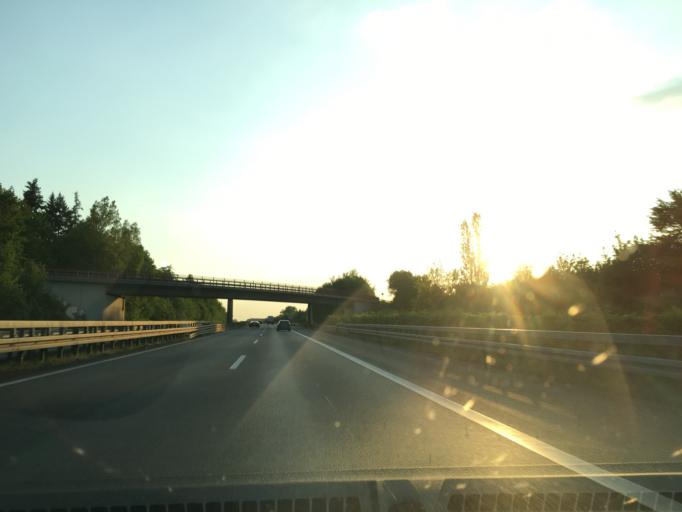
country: DE
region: North Rhine-Westphalia
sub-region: Regierungsbezirk Detmold
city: Rodinghausen
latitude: 52.1989
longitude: 8.4392
